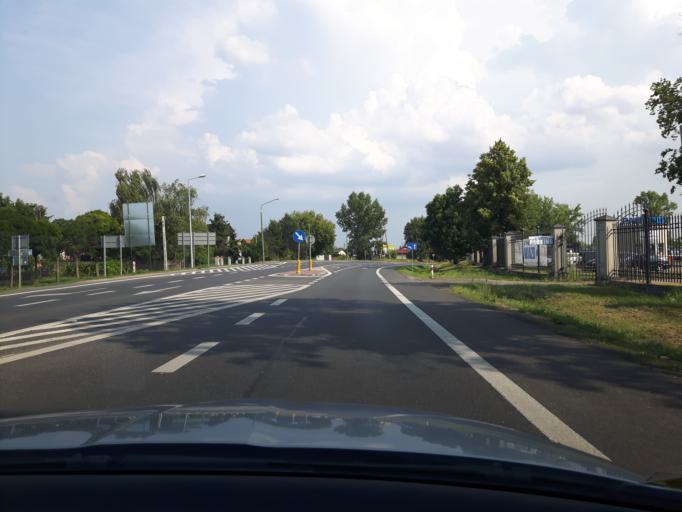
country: PL
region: Masovian Voivodeship
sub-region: Powiat nowodworski
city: Nowy Dwor Mazowiecki
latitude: 52.4461
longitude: 20.6933
